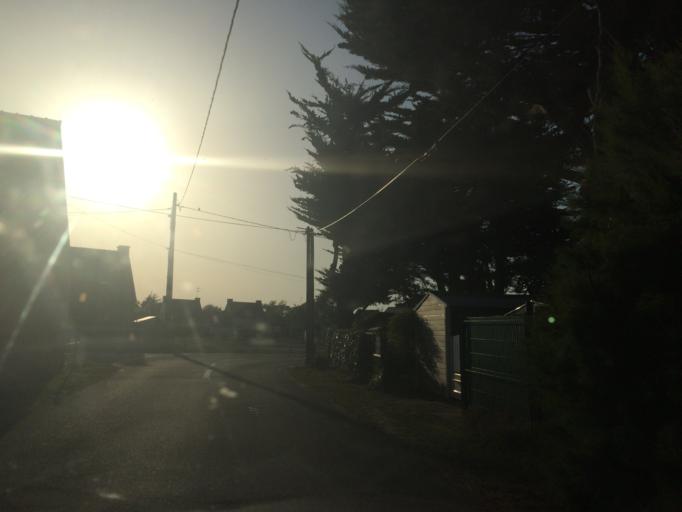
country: FR
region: Brittany
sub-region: Departement du Morbihan
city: Damgan
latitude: 47.5176
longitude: -2.5523
